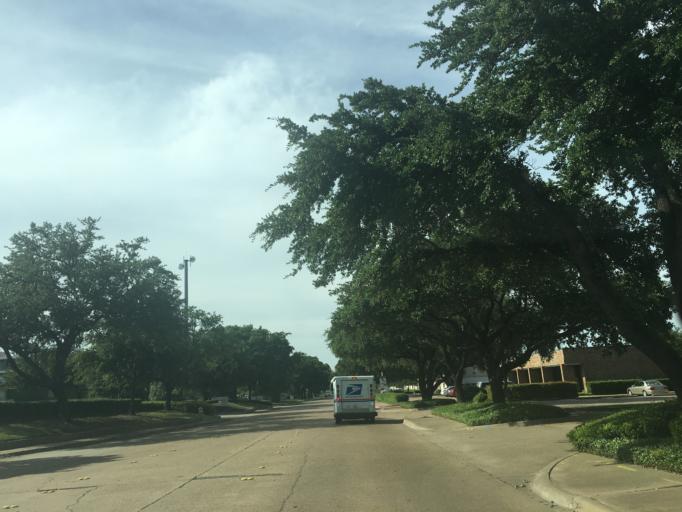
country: US
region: Texas
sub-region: Dallas County
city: Richardson
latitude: 32.9612
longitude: -96.7138
